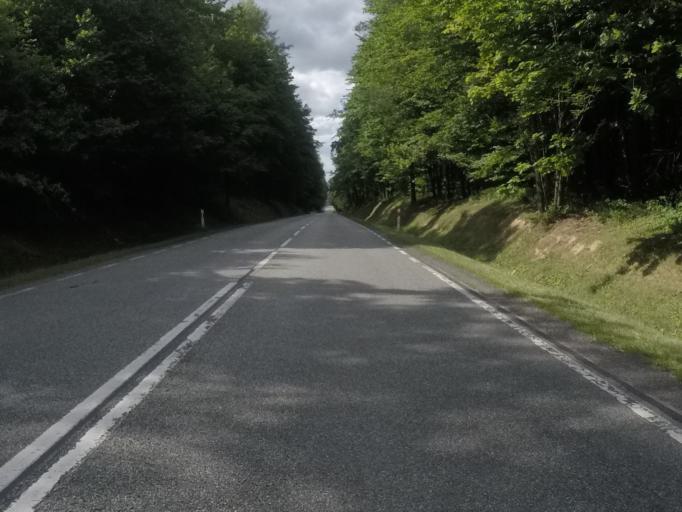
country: PL
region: Lublin Voivodeship
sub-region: Powiat krasnicki
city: Szastarka
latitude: 50.8500
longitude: 22.2895
